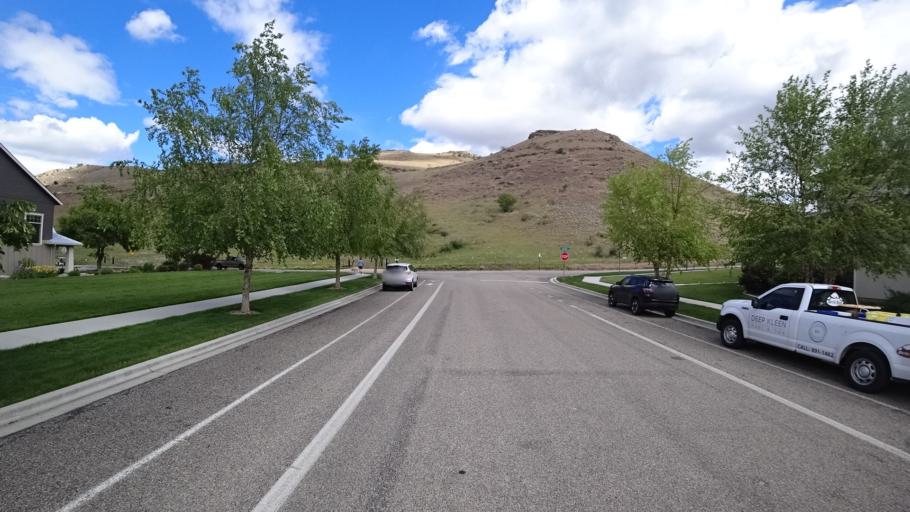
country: US
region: Idaho
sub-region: Ada County
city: Boise
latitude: 43.5802
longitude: -116.1318
